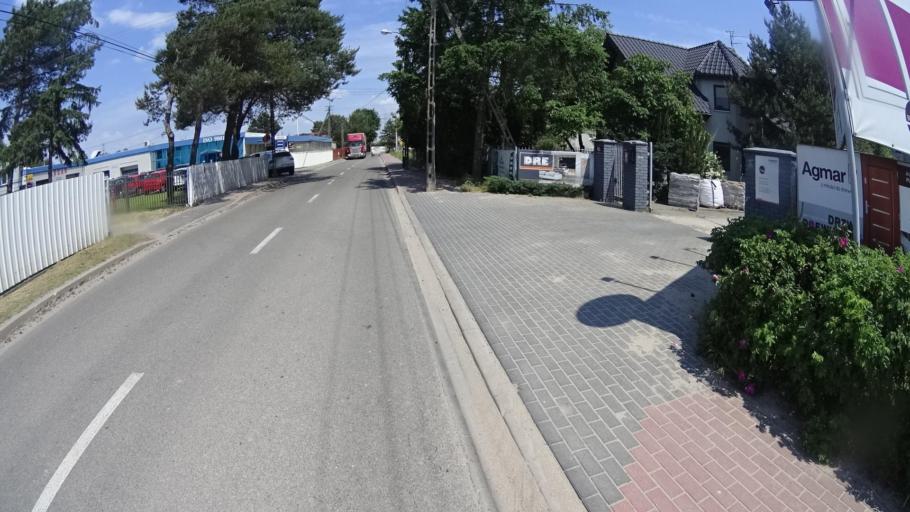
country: PL
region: Masovian Voivodeship
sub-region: Powiat warszawski zachodni
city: Stare Babice
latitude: 52.2582
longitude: 20.8330
